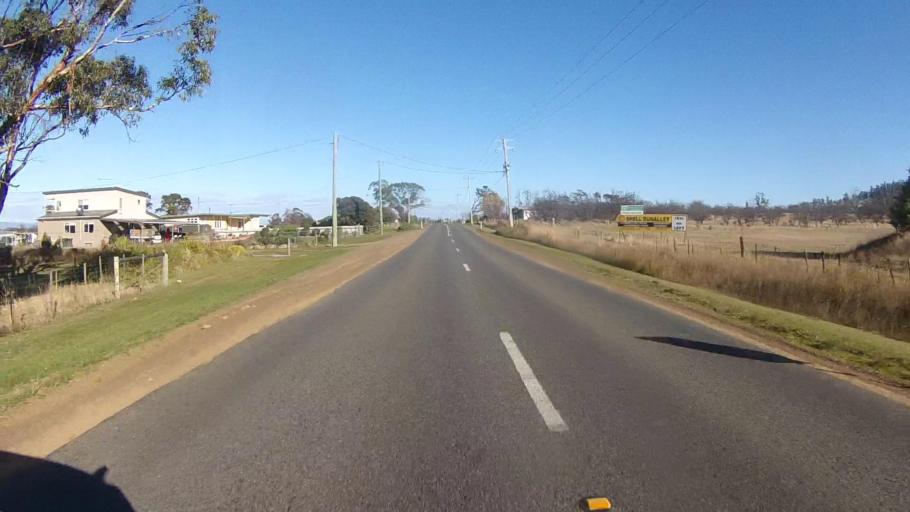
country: AU
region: Tasmania
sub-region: Sorell
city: Sorell
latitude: -42.8778
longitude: 147.8228
